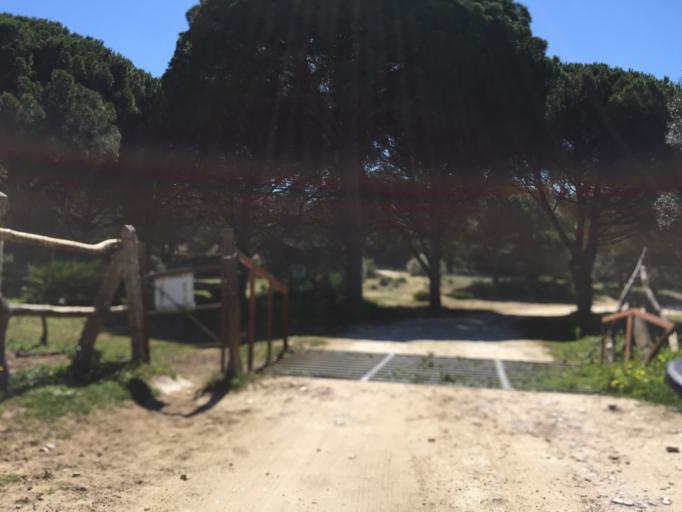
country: ES
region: Andalusia
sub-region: Provincia de Cadiz
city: Vejer de la Frontera
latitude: 36.2055
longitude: -5.9760
